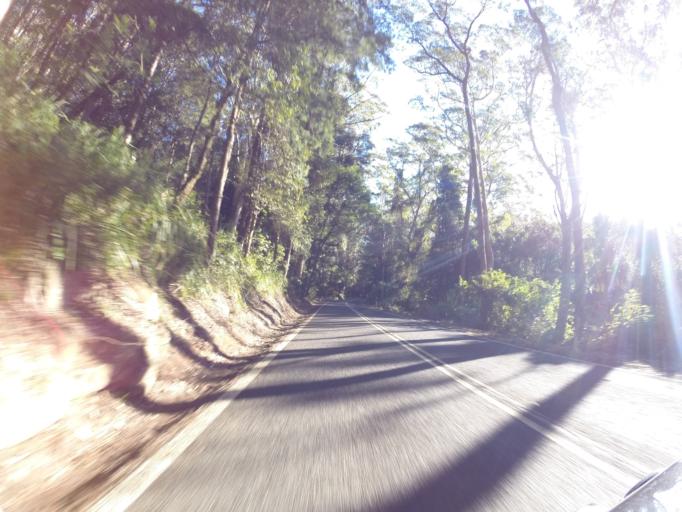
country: AU
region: New South Wales
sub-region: Wollongong
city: Helensburgh
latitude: -34.1832
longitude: 151.0117
